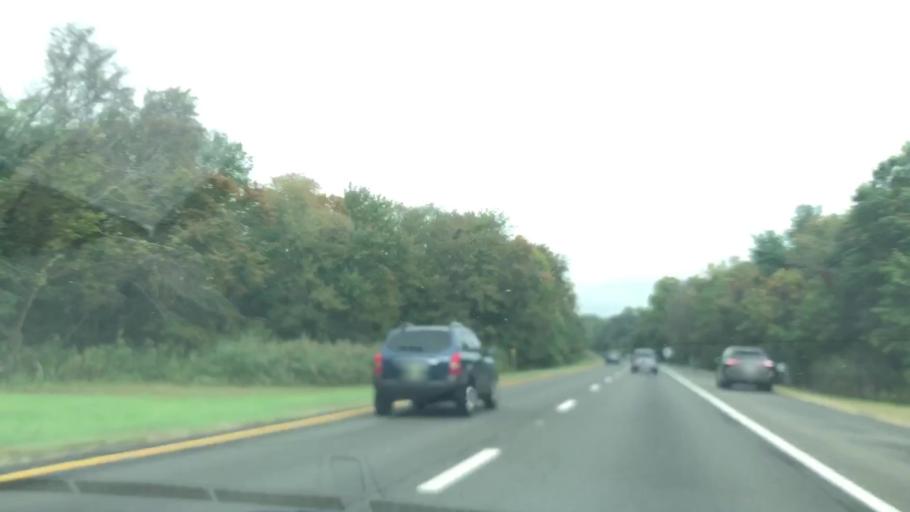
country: US
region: New Jersey
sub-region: Bergen County
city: Woodcliff Lake
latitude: 40.9990
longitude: -74.0710
